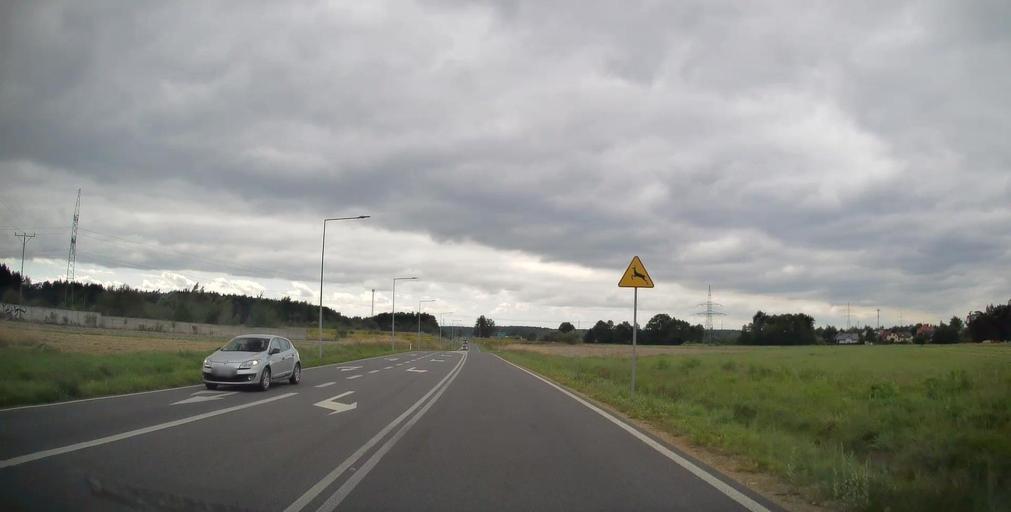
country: PL
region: Lesser Poland Voivodeship
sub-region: Powiat chrzanowski
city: Babice
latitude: 50.0651
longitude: 19.4597
